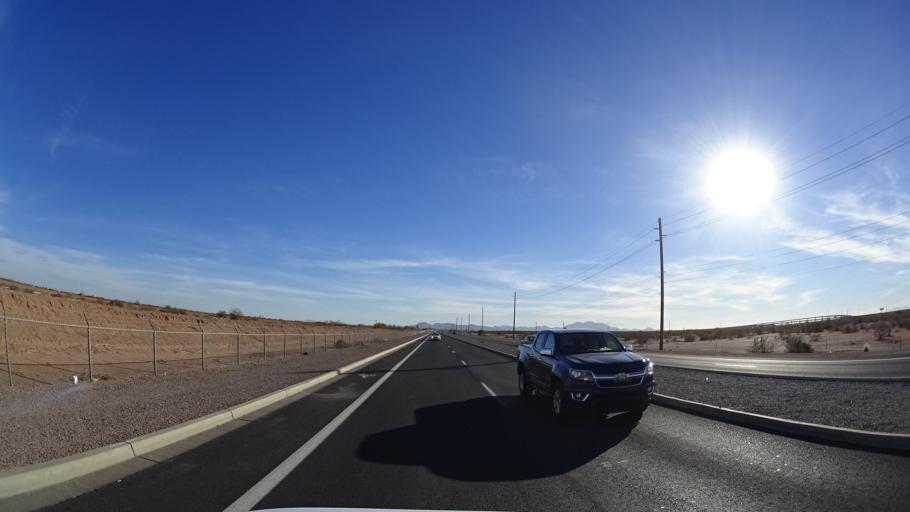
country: US
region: Arizona
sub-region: Maricopa County
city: Queen Creek
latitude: 33.3408
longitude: -111.6356
